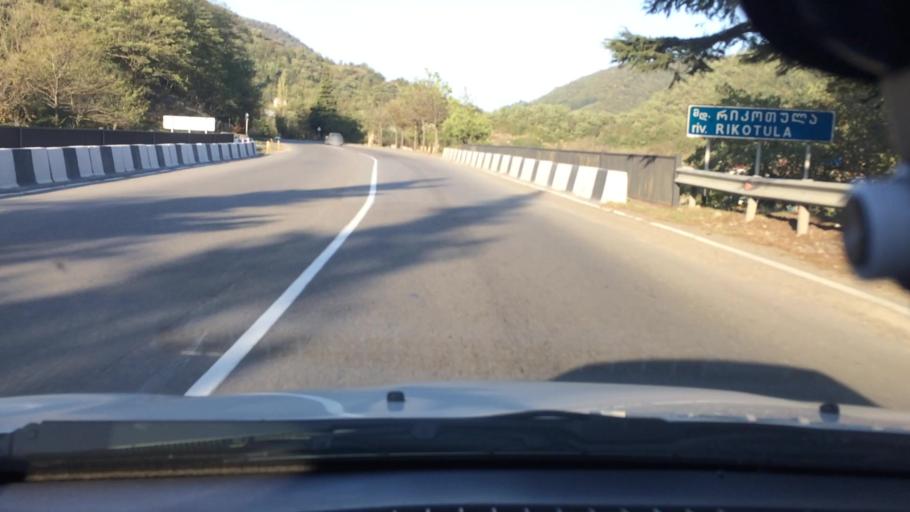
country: GE
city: Surami
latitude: 42.0974
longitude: 43.4049
